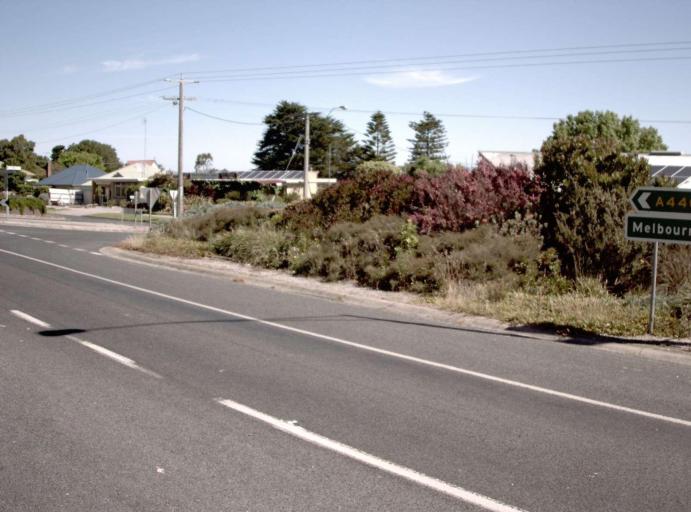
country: AU
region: Victoria
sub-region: Latrobe
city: Morwell
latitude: -38.6614
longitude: 146.3253
